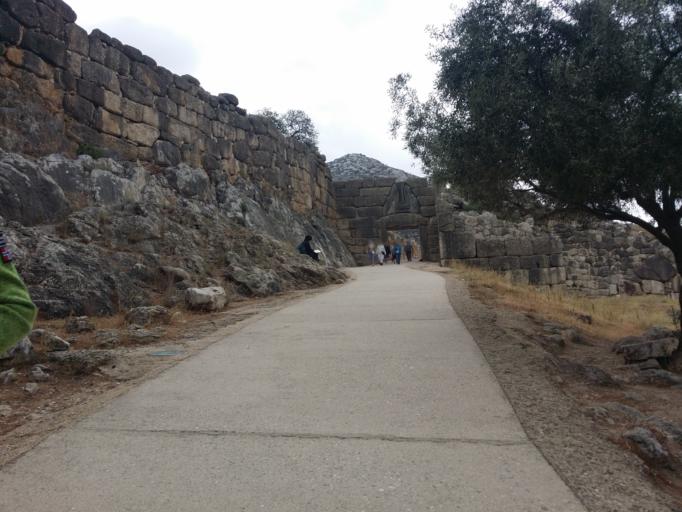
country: GR
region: Peloponnese
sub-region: Nomos Argolidos
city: Koutsopodi
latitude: 37.7312
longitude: 22.7560
